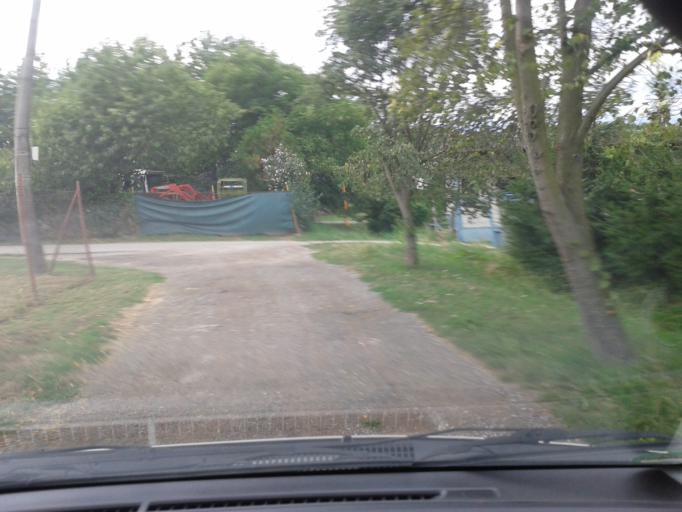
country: SK
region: Nitriansky
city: Zlate Moravce
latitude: 48.3980
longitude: 18.3538
